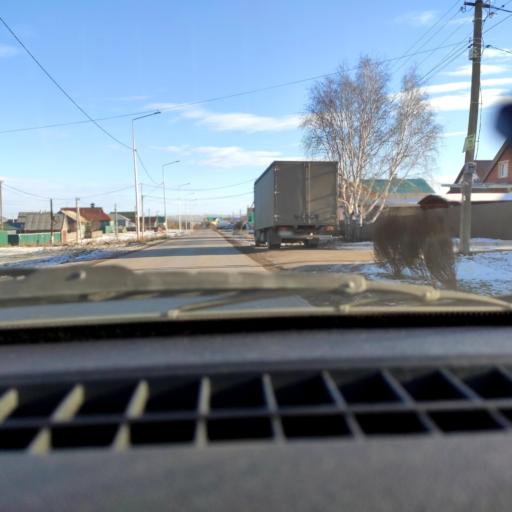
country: RU
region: Bashkortostan
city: Kabakovo
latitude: 54.5023
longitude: 55.9180
